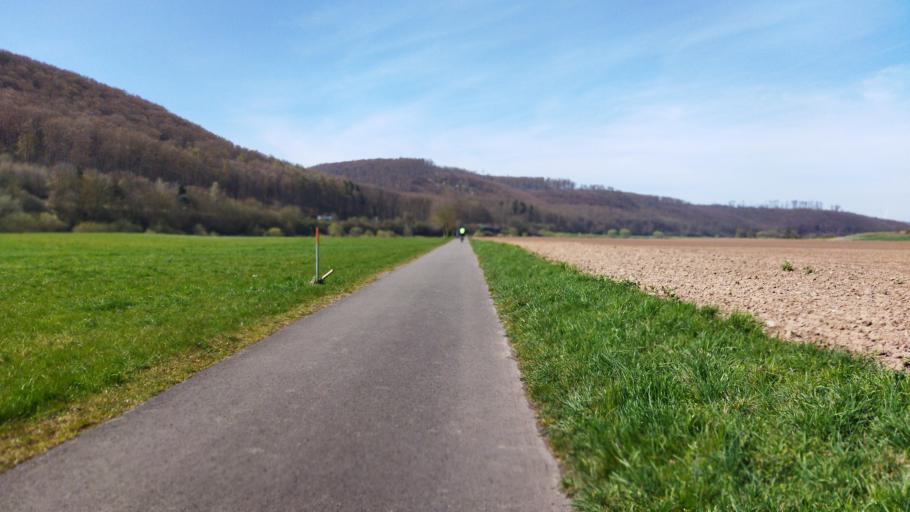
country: DE
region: Lower Saxony
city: Hehlen
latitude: 51.9857
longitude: 9.4576
